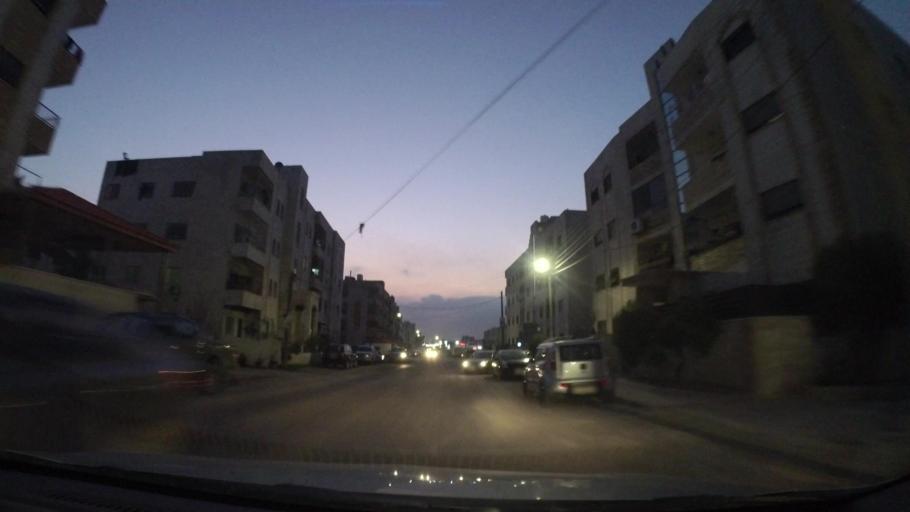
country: JO
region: Amman
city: Al Bunayyat ash Shamaliyah
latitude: 31.8949
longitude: 35.9198
